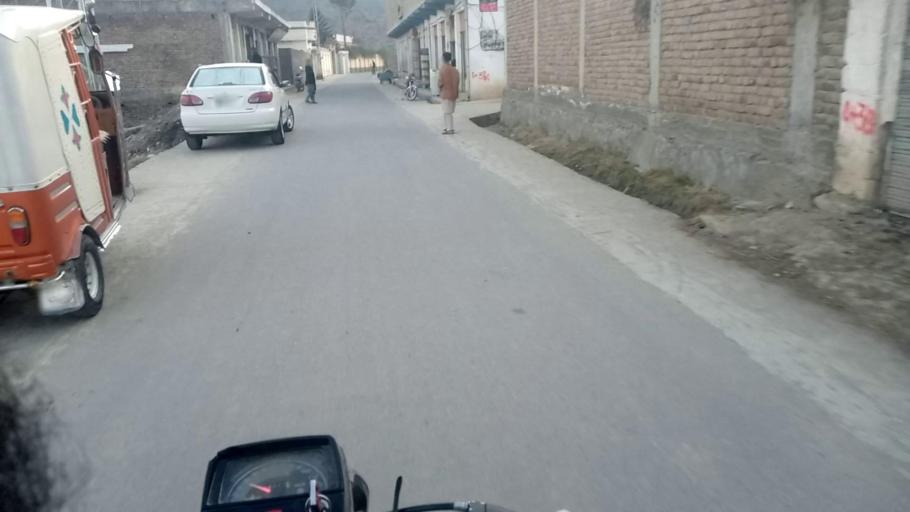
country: PK
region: Khyber Pakhtunkhwa
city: Saidu Sharif
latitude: 34.7403
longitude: 72.3374
